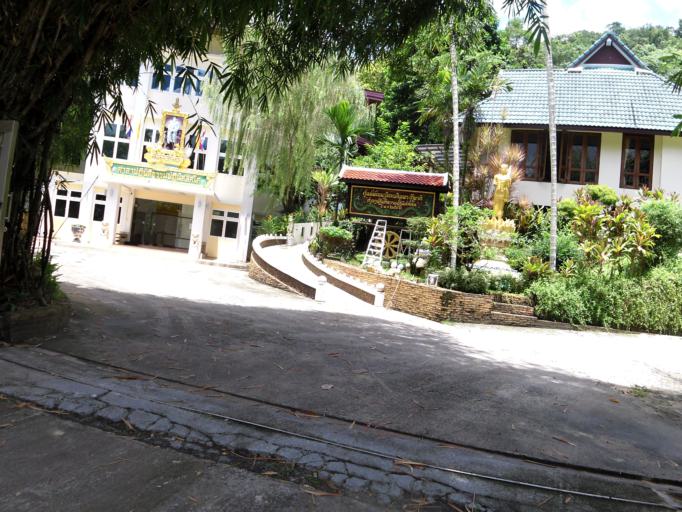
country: TH
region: Phuket
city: Ban Karon
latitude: 7.8561
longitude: 98.2941
